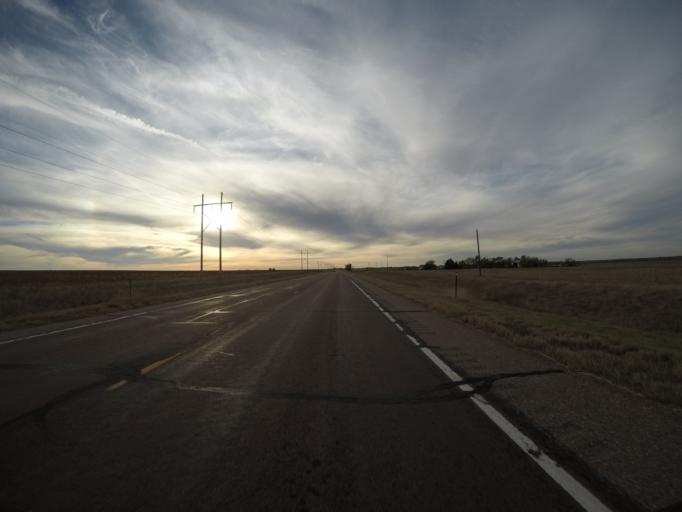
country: US
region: Colorado
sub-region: Yuma County
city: Yuma
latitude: 39.6551
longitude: -102.8228
